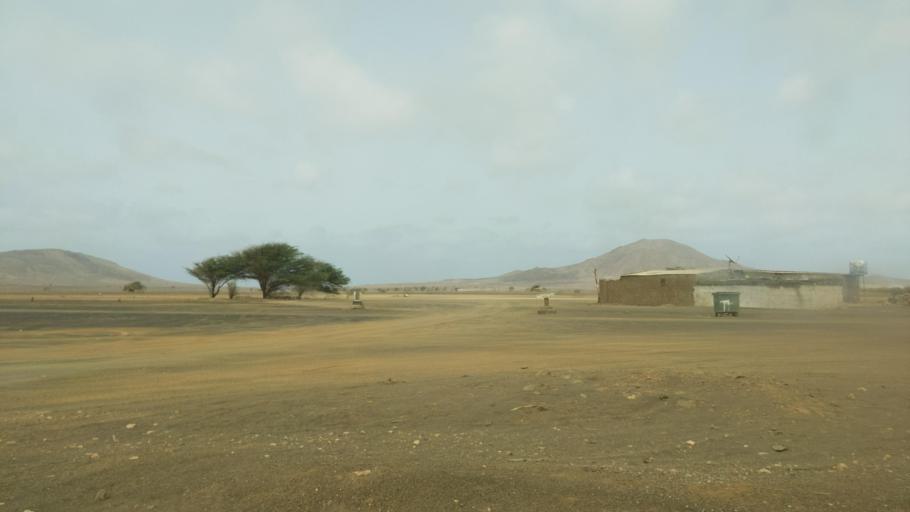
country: CV
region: Sal
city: Espargos
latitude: 16.7947
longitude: -22.9517
